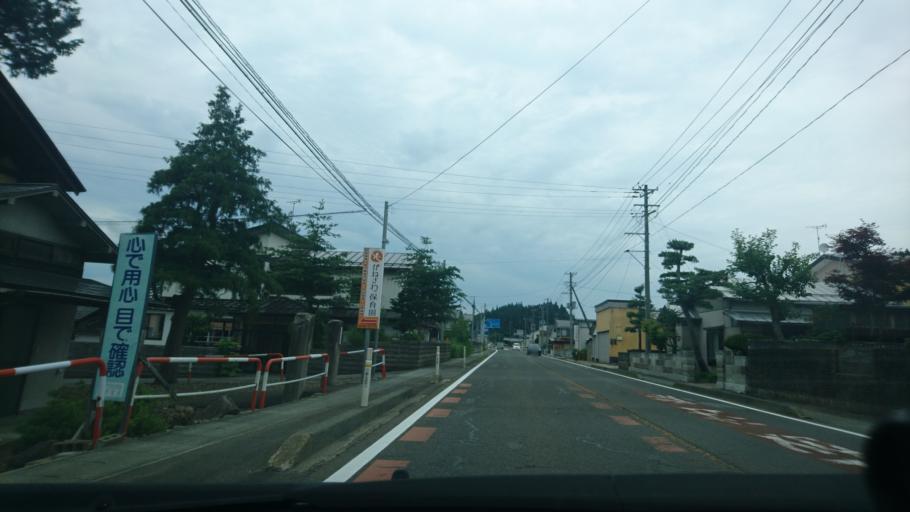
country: JP
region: Akita
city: Yokotemachi
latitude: 39.3697
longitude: 140.5683
